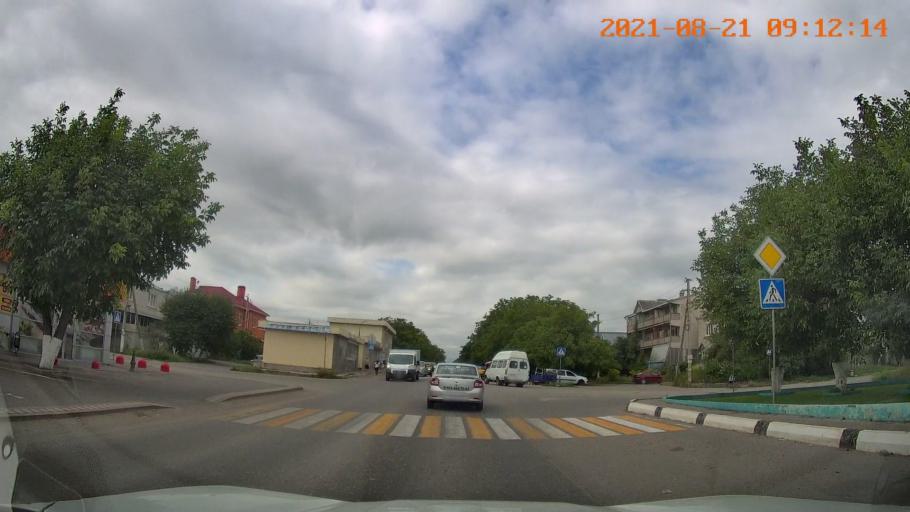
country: RU
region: Stavropol'skiy
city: Svobody
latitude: 44.0142
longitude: 43.0651
